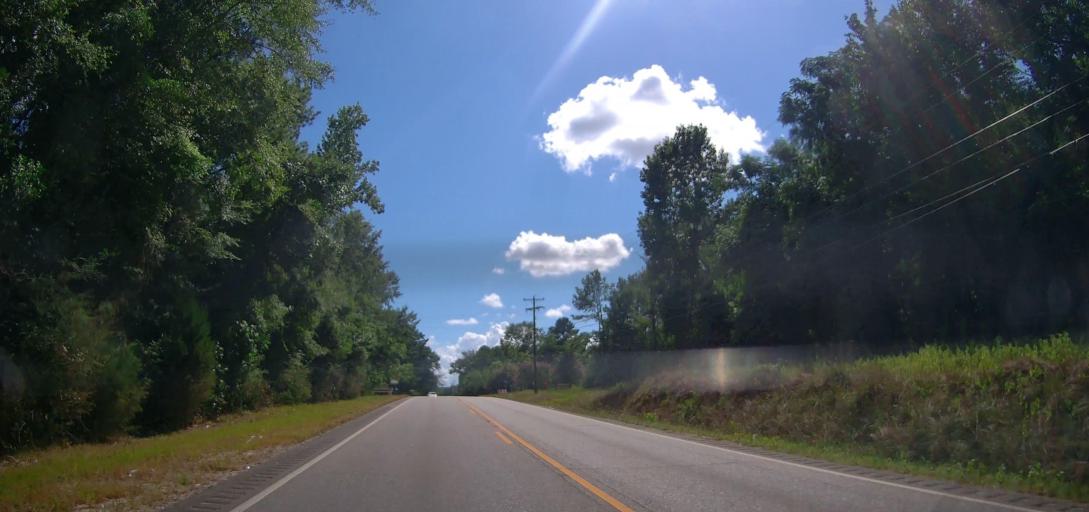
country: US
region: Alabama
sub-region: Macon County
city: Tuskegee
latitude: 32.4327
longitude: -85.6754
